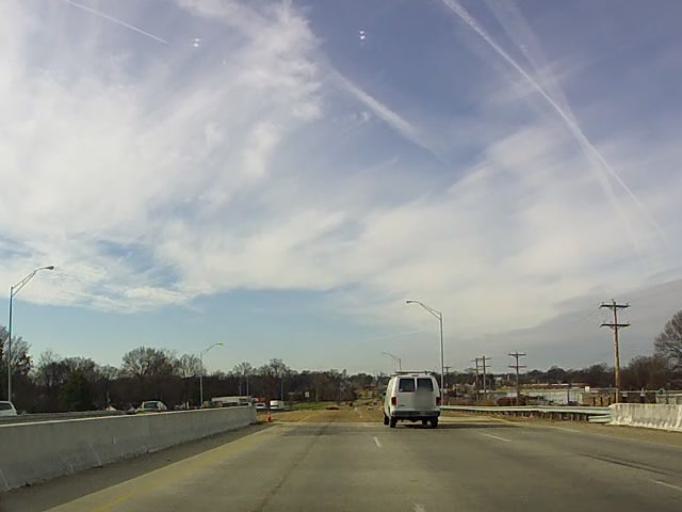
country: US
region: Tennessee
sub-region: Shelby County
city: Memphis
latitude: 35.1475
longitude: -89.9554
